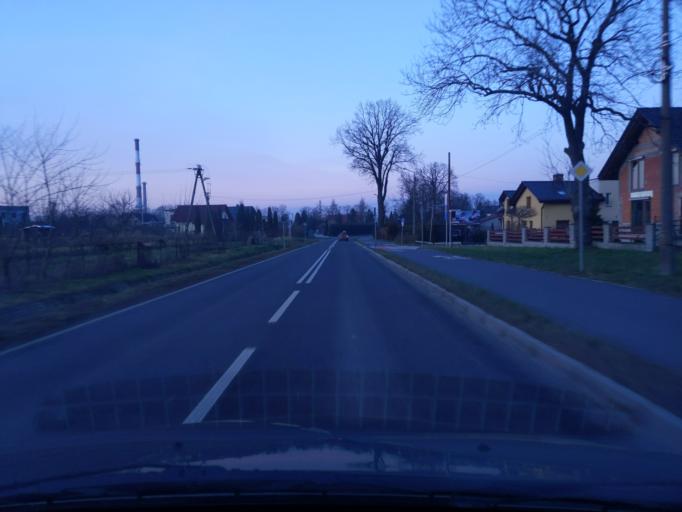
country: PL
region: Silesian Voivodeship
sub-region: Powiat pszczynski
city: Pszczyna
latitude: 49.9565
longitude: 18.9334
